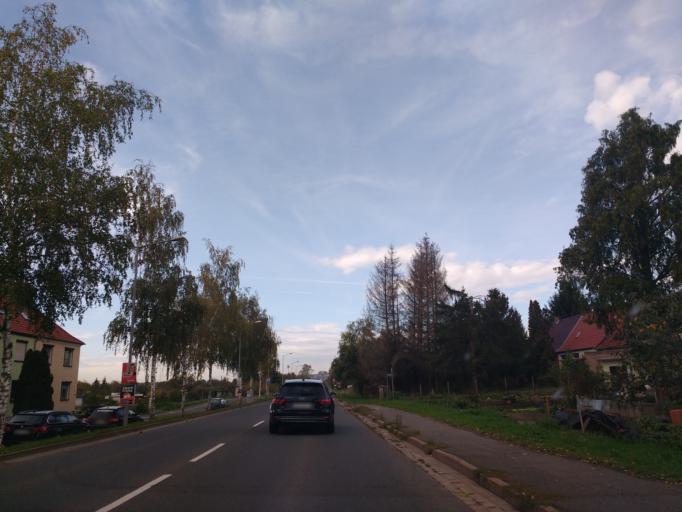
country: DE
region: Thuringia
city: Uthleben
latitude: 51.4864
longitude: 10.8396
